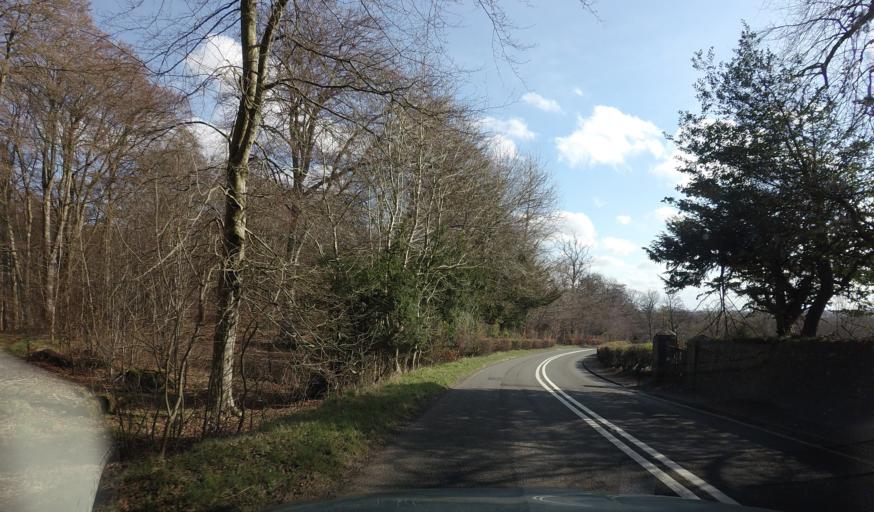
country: GB
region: Scotland
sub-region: Midlothian
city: Penicuik
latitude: 55.8273
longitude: -3.2401
